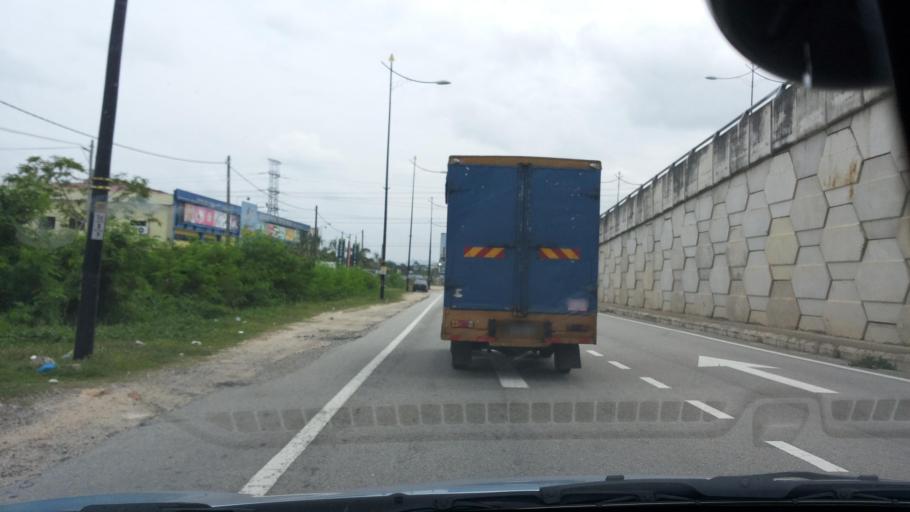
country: MY
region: Pahang
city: Kuantan
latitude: 3.7717
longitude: 103.2567
